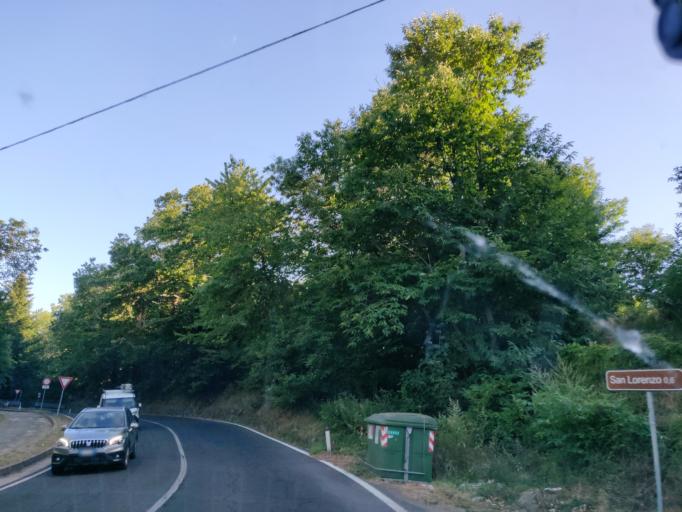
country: IT
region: Tuscany
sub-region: Provincia di Siena
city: Piancastagnaio
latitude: 42.8579
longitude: 11.6835
